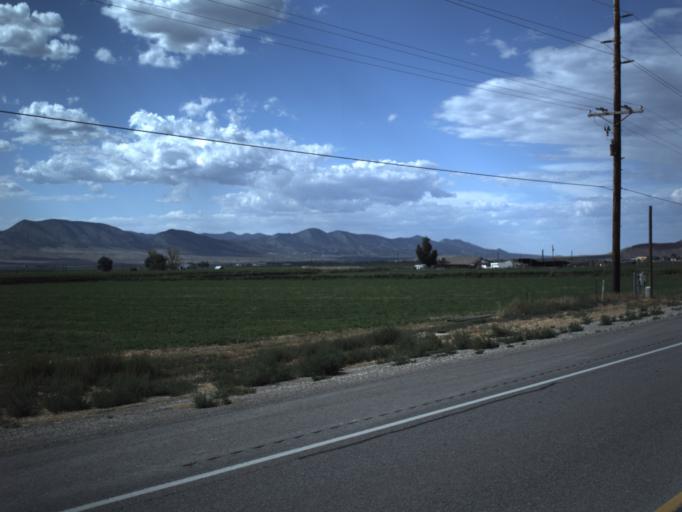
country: US
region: Utah
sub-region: Sanpete County
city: Centerfield
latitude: 39.1046
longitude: -111.8197
